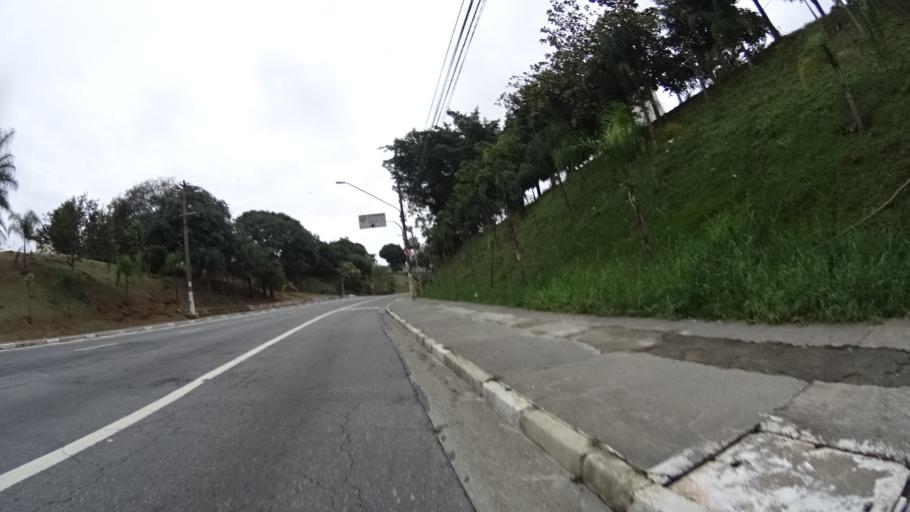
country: BR
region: Sao Paulo
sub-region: Sao Paulo
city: Sao Paulo
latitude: -23.4829
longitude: -46.6061
